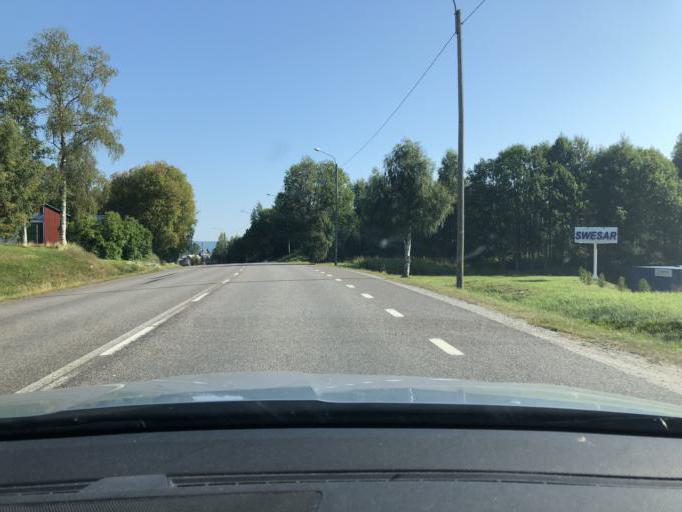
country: SE
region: Vaesternorrland
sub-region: Kramfors Kommun
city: Kramfors
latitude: 62.8784
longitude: 17.8659
